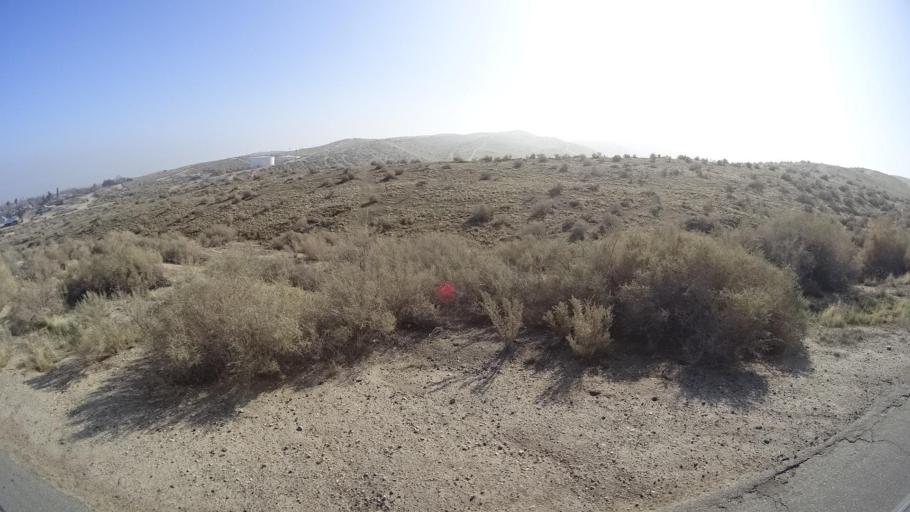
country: US
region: California
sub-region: Kern County
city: Taft Heights
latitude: 35.1301
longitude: -119.4693
